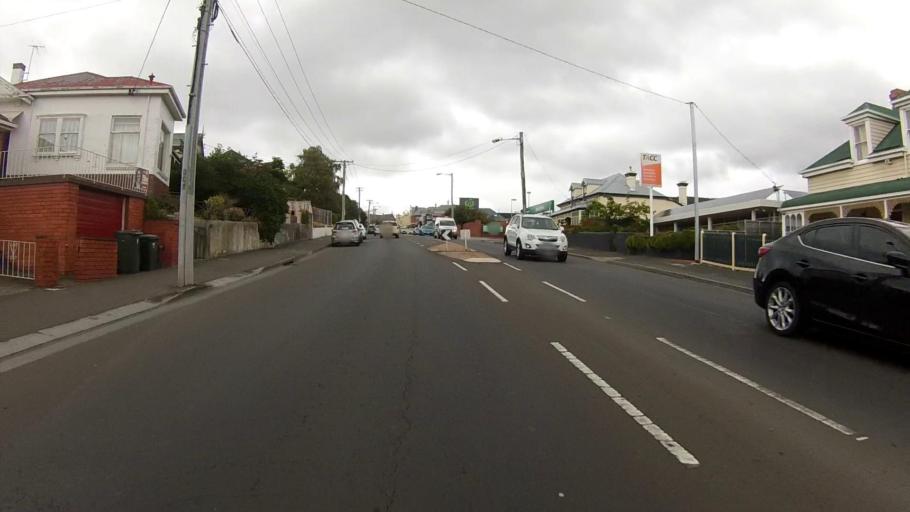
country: AU
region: Tasmania
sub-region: Hobart
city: New Town
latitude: -42.8566
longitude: 147.3038
